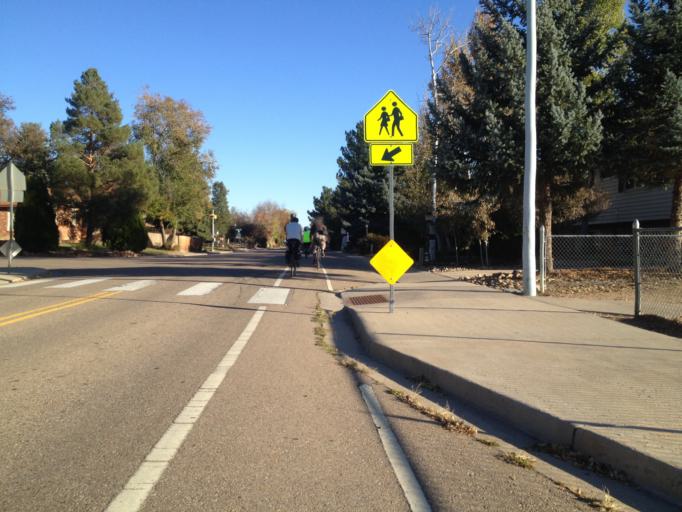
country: US
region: Colorado
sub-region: Boulder County
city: Longmont
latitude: 40.1855
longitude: -105.1467
